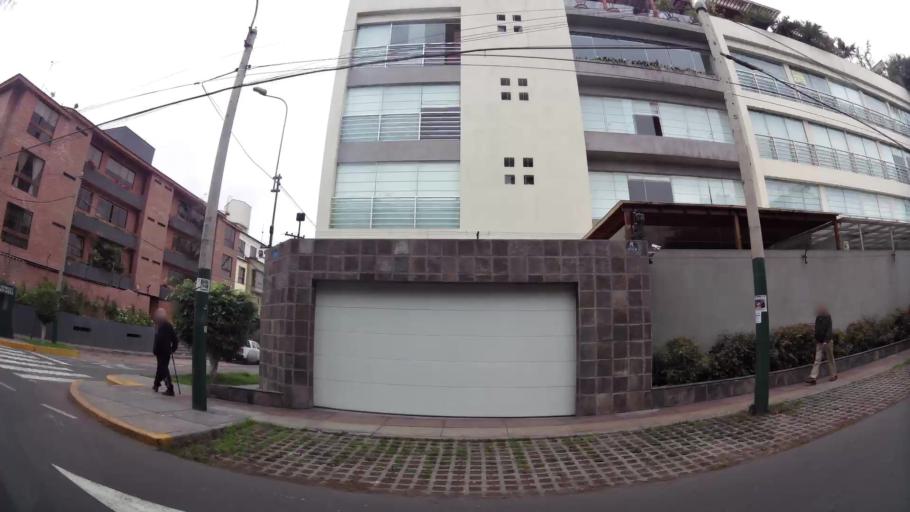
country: PE
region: Lima
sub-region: Lima
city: Surco
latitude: -12.1194
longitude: -76.9850
